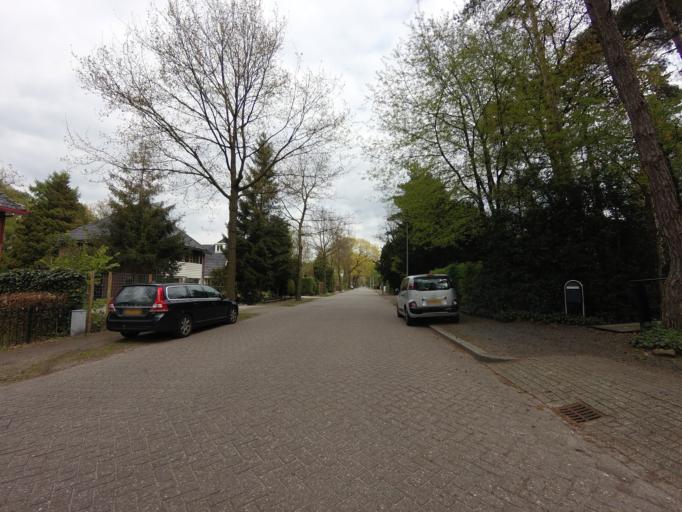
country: NL
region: Utrecht
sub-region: Gemeente Zeist
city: Zeist
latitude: 52.1361
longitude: 5.2350
